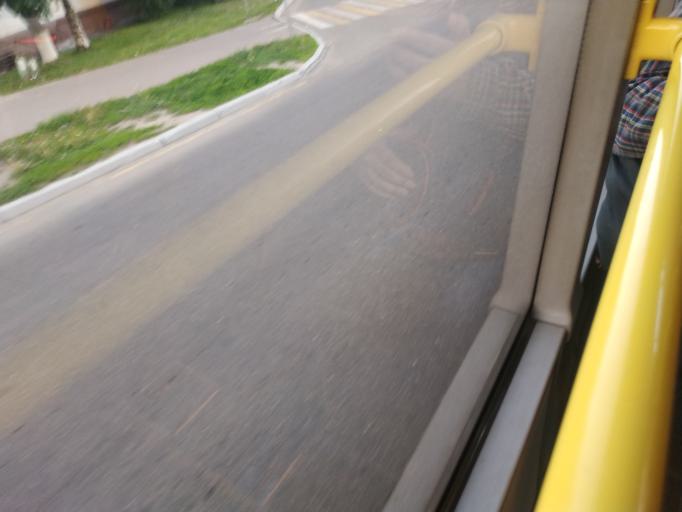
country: RU
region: Moskovskaya
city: Domodedovo
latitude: 55.4398
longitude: 37.7706
